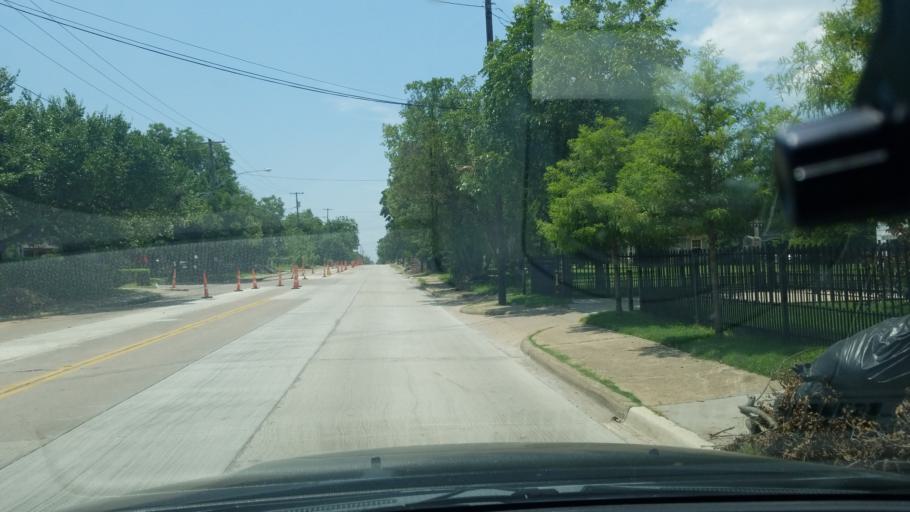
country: US
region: Texas
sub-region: Dallas County
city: Balch Springs
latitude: 32.7410
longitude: -96.6786
